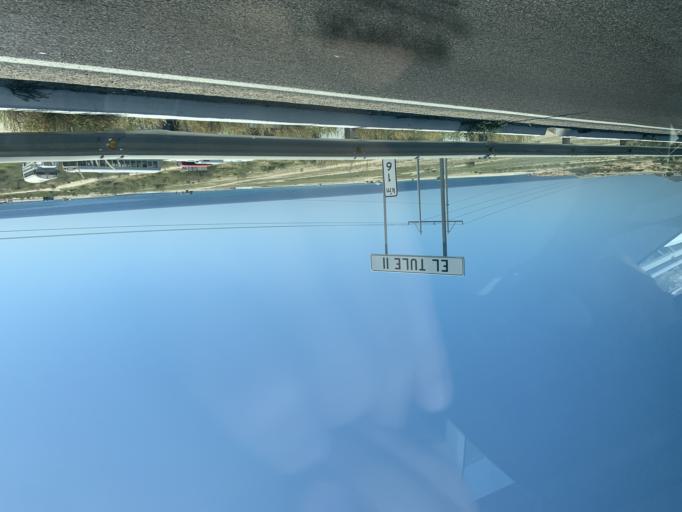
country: MX
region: Baja California Sur
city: Cabo San Lucas
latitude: 22.9605
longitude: -109.8034
